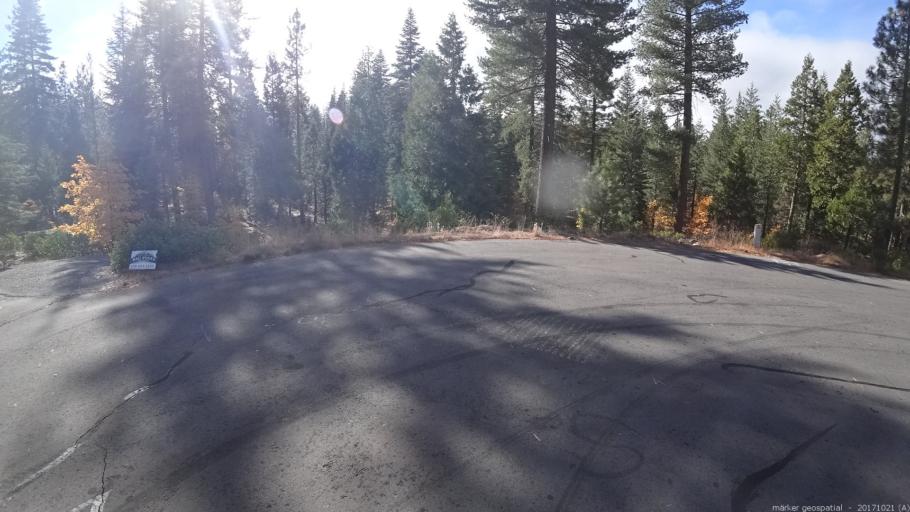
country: US
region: California
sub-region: Shasta County
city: Burney
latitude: 40.8723
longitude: -121.6580
